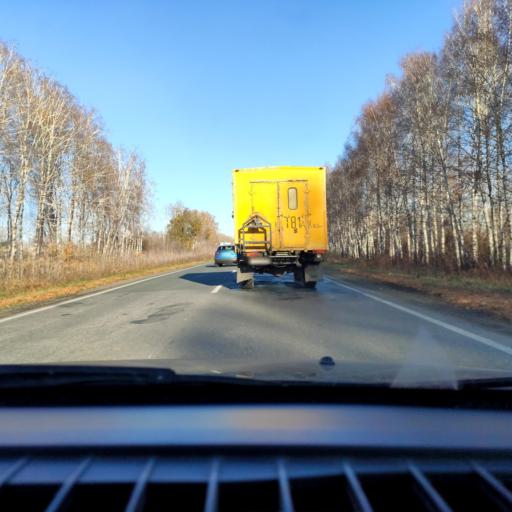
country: RU
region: Samara
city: Tol'yatti
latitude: 53.5943
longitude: 49.3268
